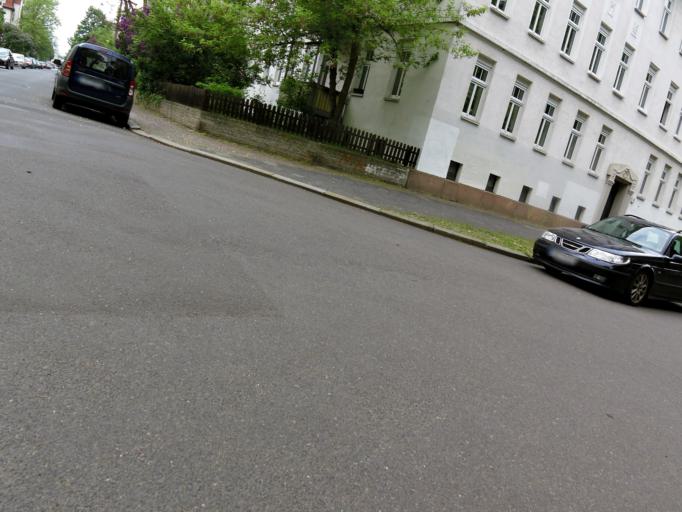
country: DE
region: Saxony
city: Markkleeberg
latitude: 51.3068
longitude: 12.3855
